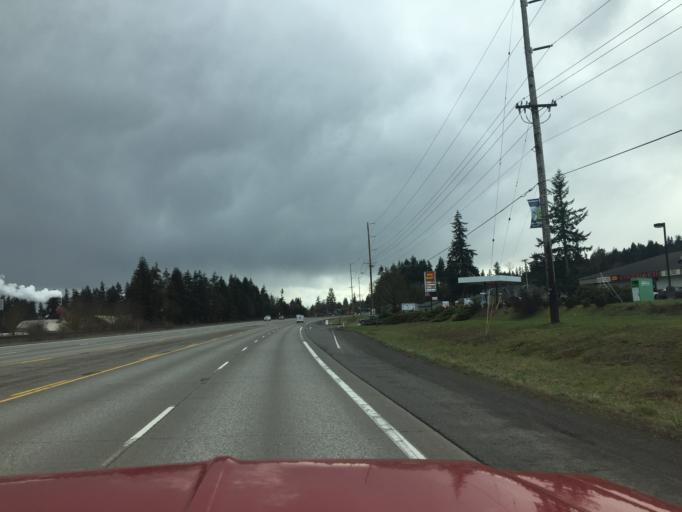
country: US
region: Oregon
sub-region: Columbia County
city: Columbia City
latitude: 45.8983
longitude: -122.8137
